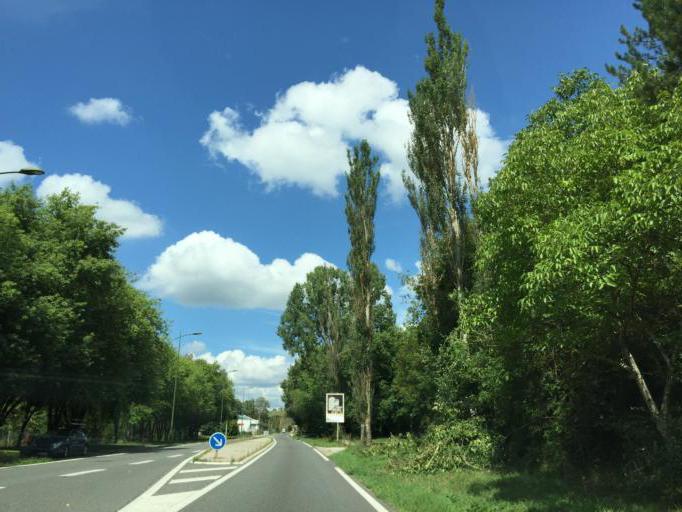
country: FR
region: Midi-Pyrenees
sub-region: Departement de l'Aveyron
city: Rodez
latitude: 44.3780
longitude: 2.5657
